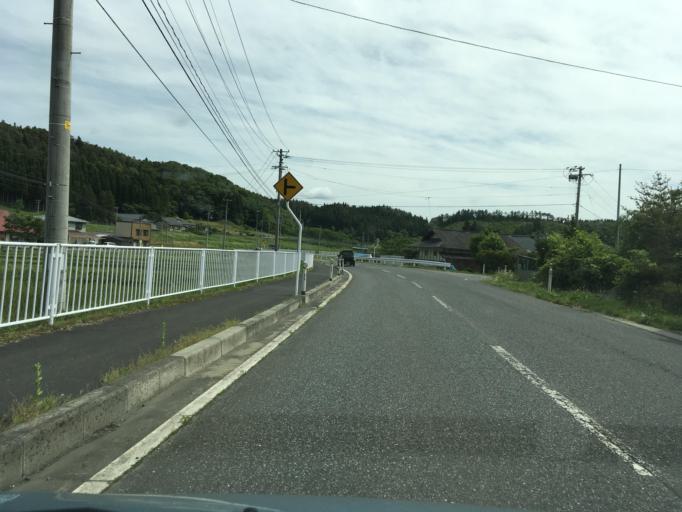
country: JP
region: Iwate
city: Mizusawa
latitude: 39.0813
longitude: 141.3535
